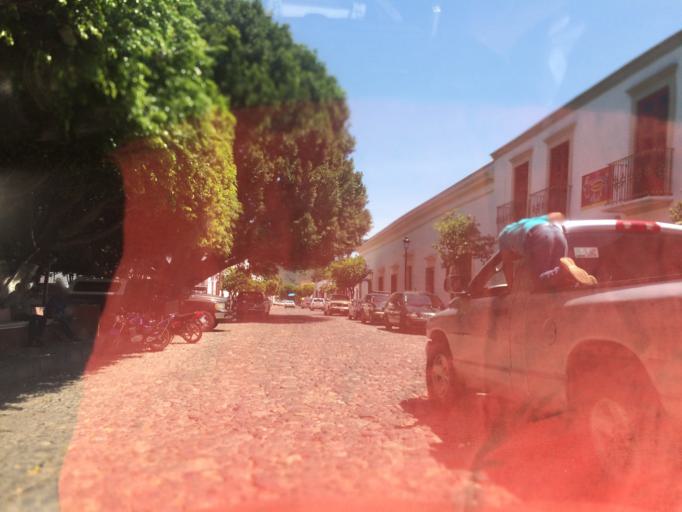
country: MX
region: Nayarit
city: Jala
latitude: 21.1045
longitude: -104.4381
